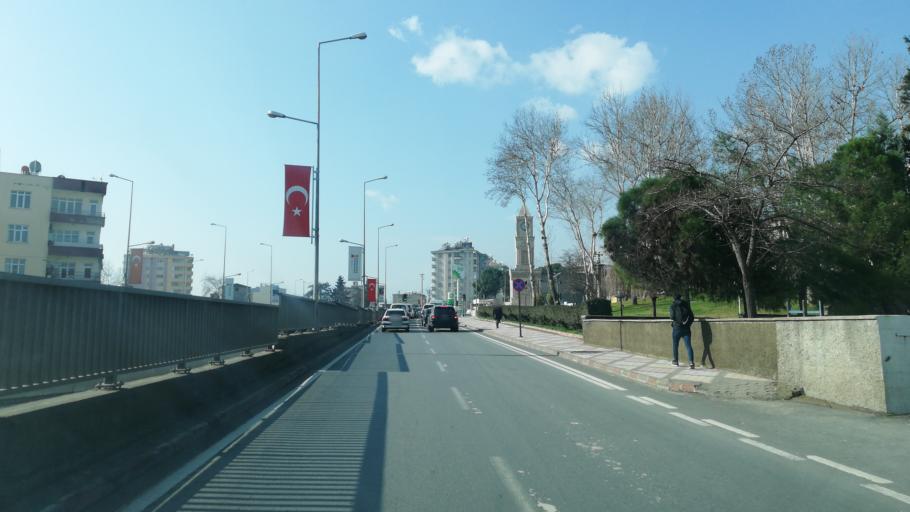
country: TR
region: Kahramanmaras
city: Kahramanmaras
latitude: 37.5707
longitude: 36.9442
